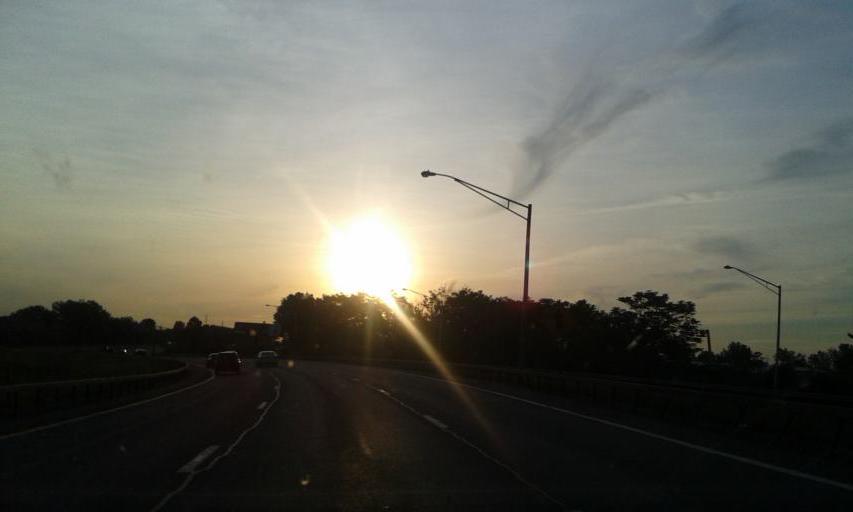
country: US
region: New York
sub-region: Onondaga County
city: Syracuse
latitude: 43.0568
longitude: -76.1762
